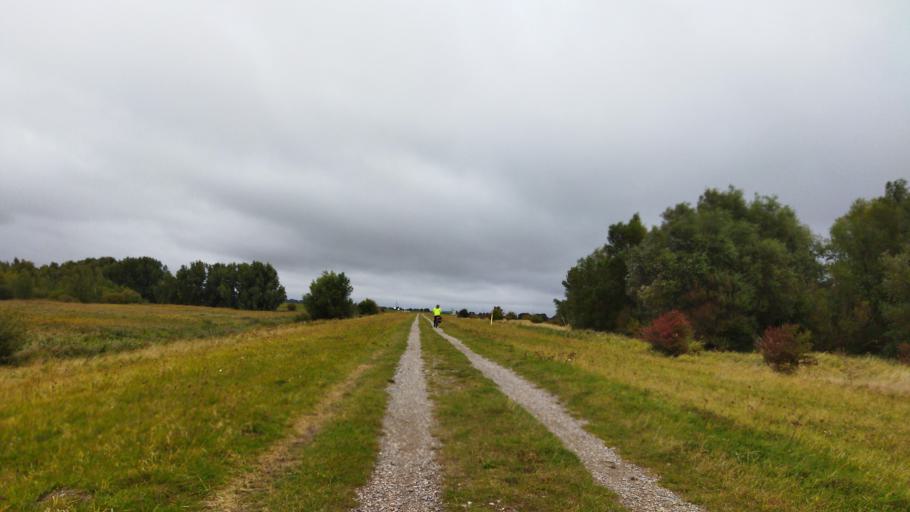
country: NL
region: Groningen
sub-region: Gemeente Delfzijl
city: Delfzijl
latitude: 53.3760
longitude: 7.0126
